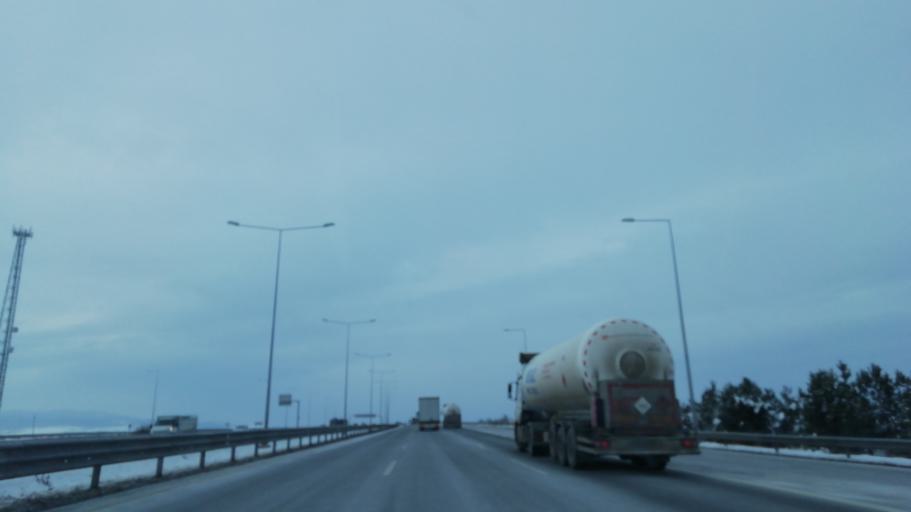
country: TR
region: Bolu
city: Dortdivan
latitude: 40.7440
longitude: 32.1180
